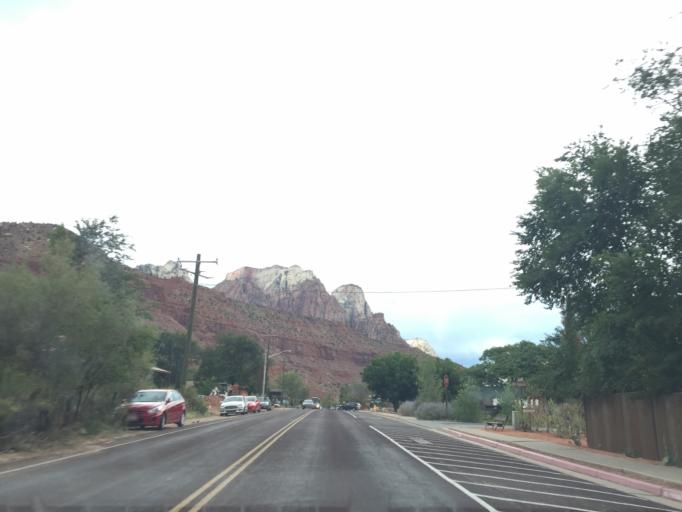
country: US
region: Utah
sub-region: Washington County
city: Hildale
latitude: 37.1928
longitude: -112.9935
